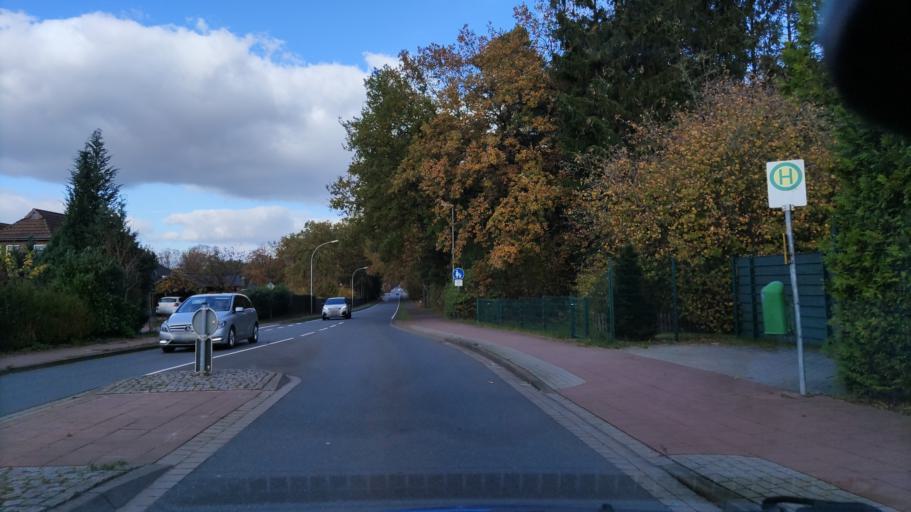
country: DE
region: Lower Saxony
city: Munster
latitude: 53.0068
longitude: 10.0882
